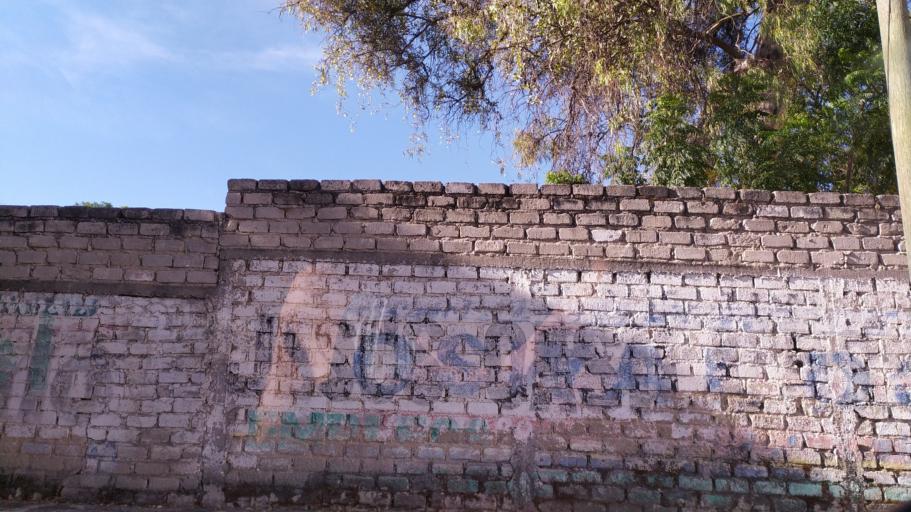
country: MX
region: Jalisco
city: Guadalajara
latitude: 20.6612
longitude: -103.4362
